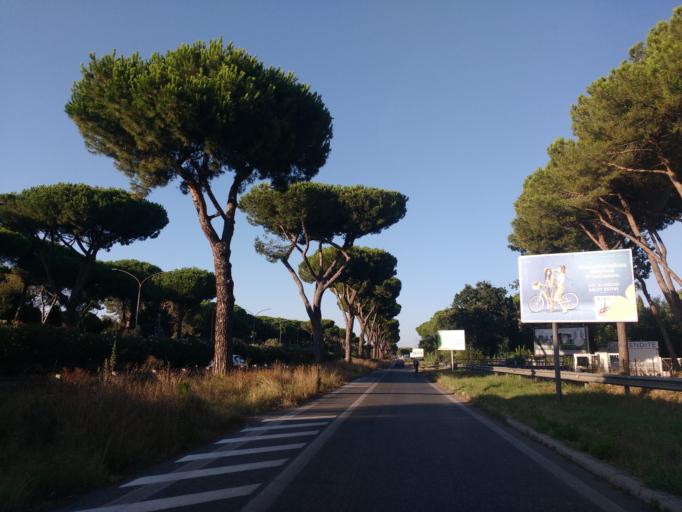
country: IT
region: Latium
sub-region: Citta metropolitana di Roma Capitale
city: Acilia-Castel Fusano-Ostia Antica
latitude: 41.7475
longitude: 12.3604
